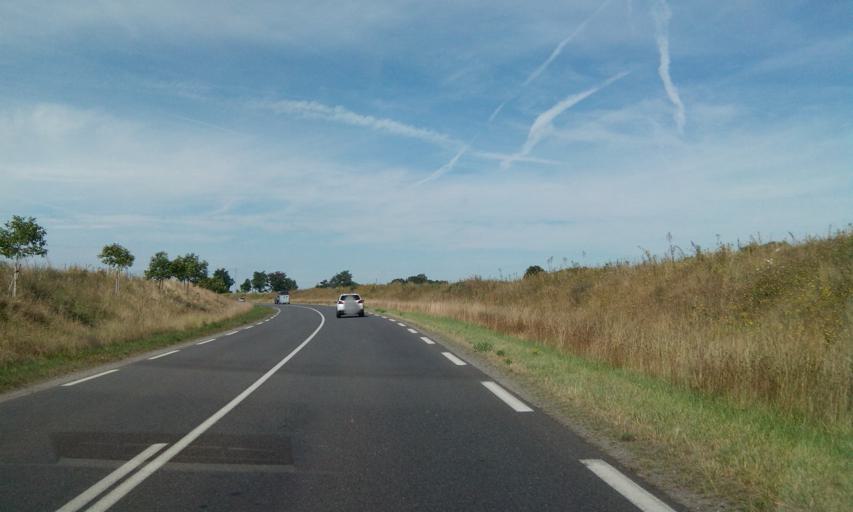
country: FR
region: Poitou-Charentes
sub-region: Departement de la Vienne
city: Charroux
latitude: 46.1548
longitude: 0.3850
